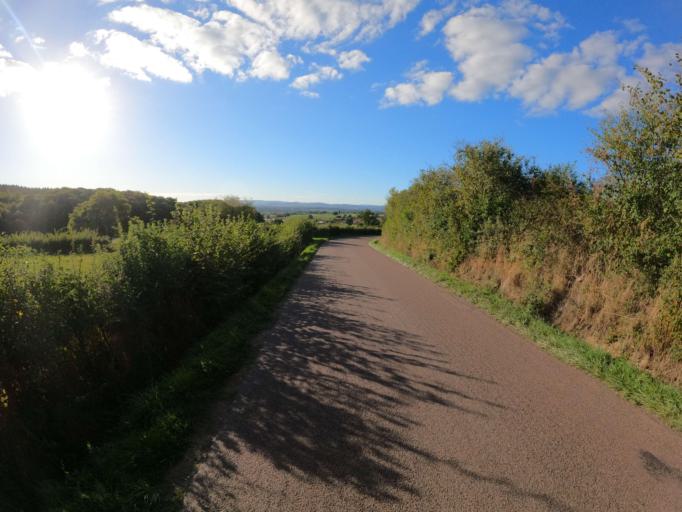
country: FR
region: Bourgogne
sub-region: Departement de Saone-et-Loire
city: Ecuisses
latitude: 46.7407
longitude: 4.5465
